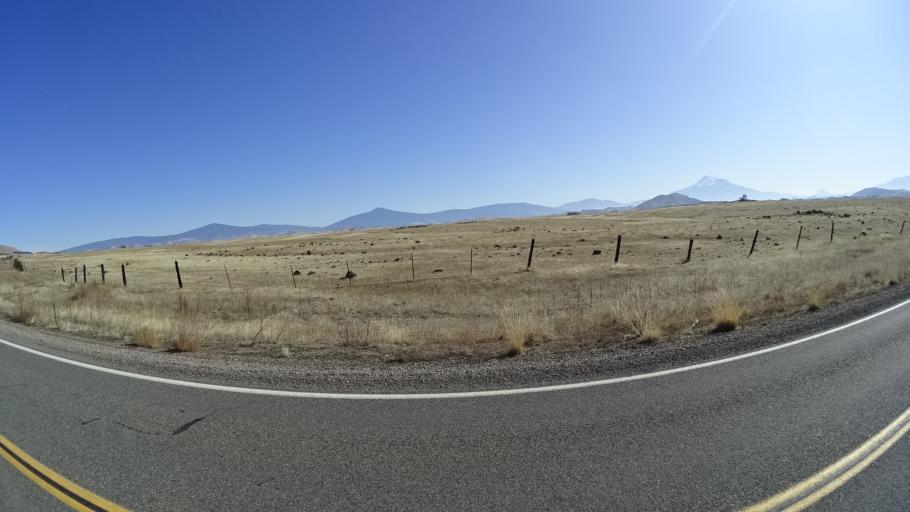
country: US
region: California
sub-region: Siskiyou County
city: Montague
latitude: 41.7604
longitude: -122.5736
